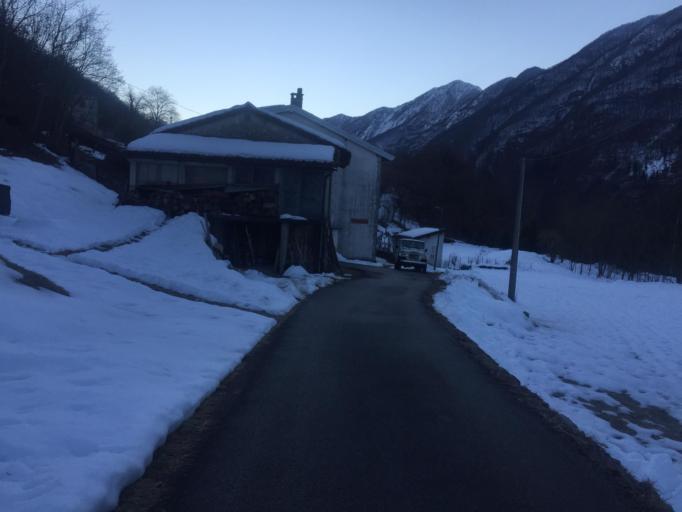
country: IT
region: Friuli Venezia Giulia
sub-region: Provincia di Udine
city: Chiaulis
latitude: 46.3730
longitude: 12.9748
